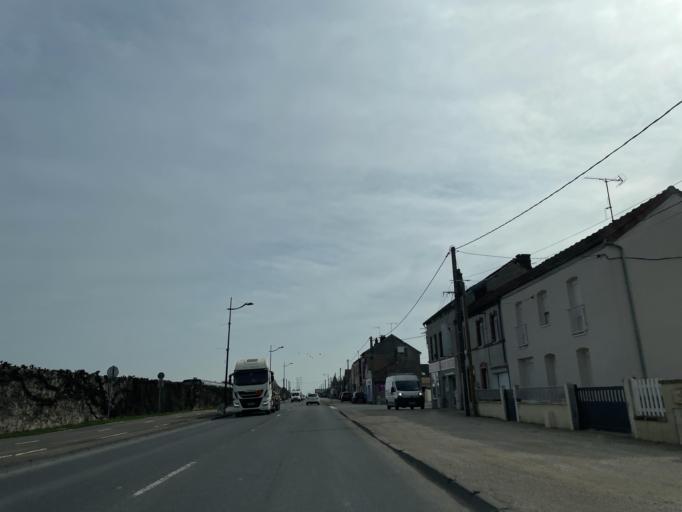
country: FR
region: Champagne-Ardenne
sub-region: Departement de l'Aube
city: Romilly-sur-Seine
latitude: 48.5084
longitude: 3.7379
